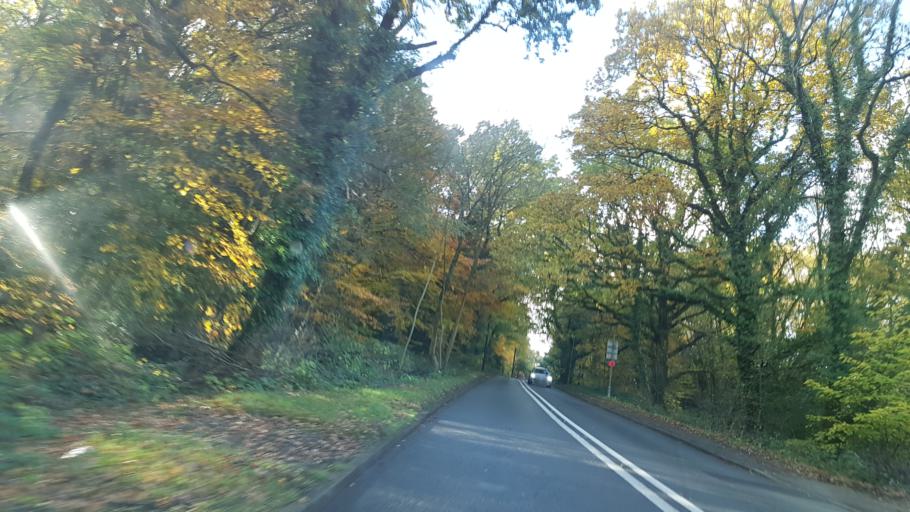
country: GB
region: England
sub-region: Surrey
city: Haslemere
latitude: 51.1027
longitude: -0.6928
